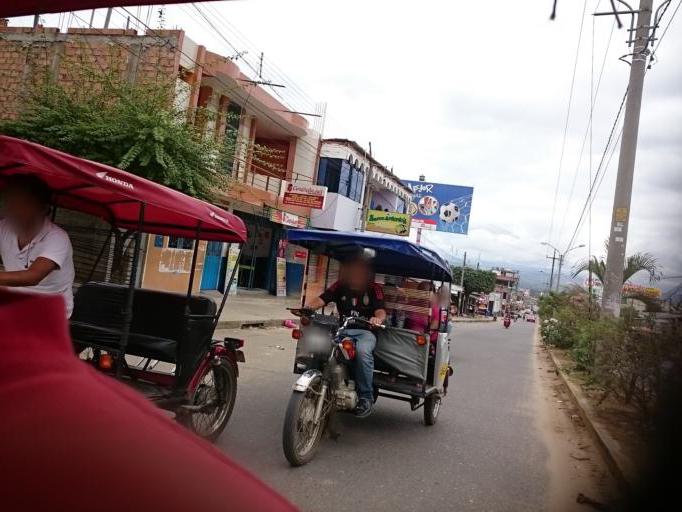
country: PE
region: San Martin
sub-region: Provincia de San Martin
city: Tarapoto
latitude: -6.4906
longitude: -76.3676
